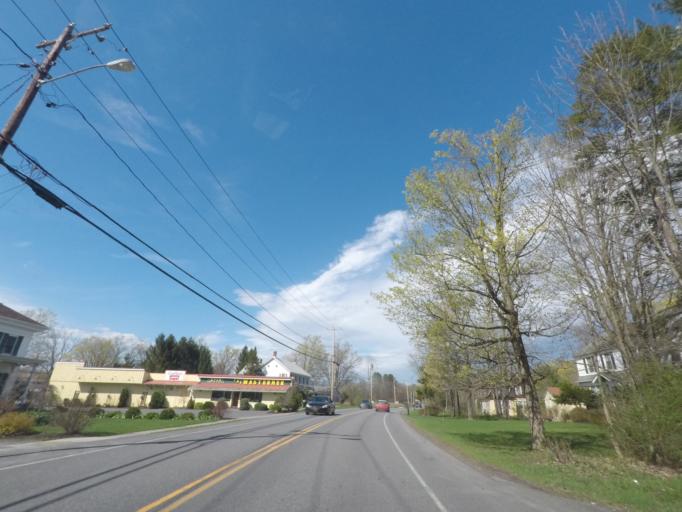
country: US
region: New York
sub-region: Greene County
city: Cairo
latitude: 42.4200
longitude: -74.0212
